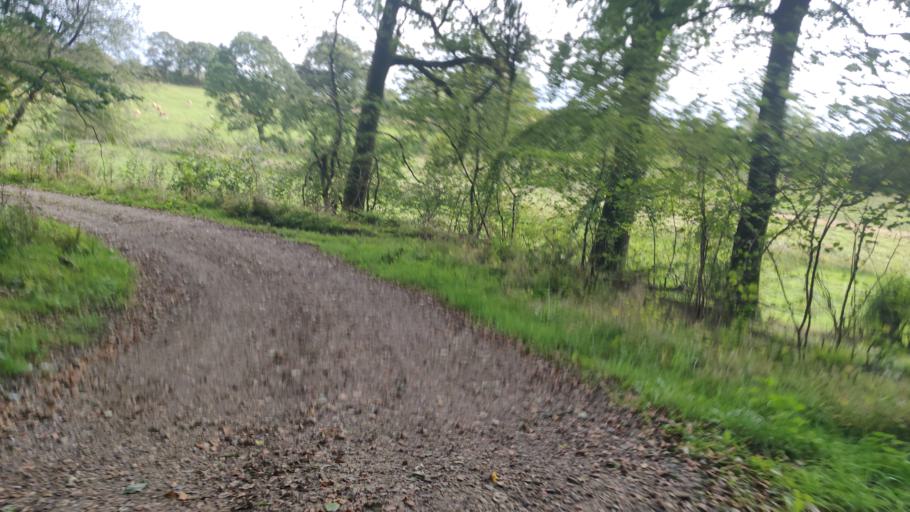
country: DK
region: South Denmark
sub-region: Kolding Kommune
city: Lunderskov
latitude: 55.5417
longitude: 9.3653
